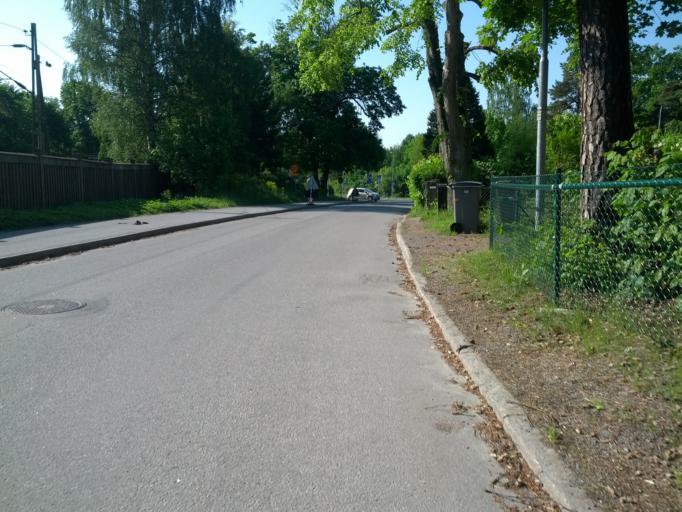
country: SE
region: Stockholm
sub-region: Danderyds Kommun
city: Djursholm
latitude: 59.4108
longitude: 18.0584
